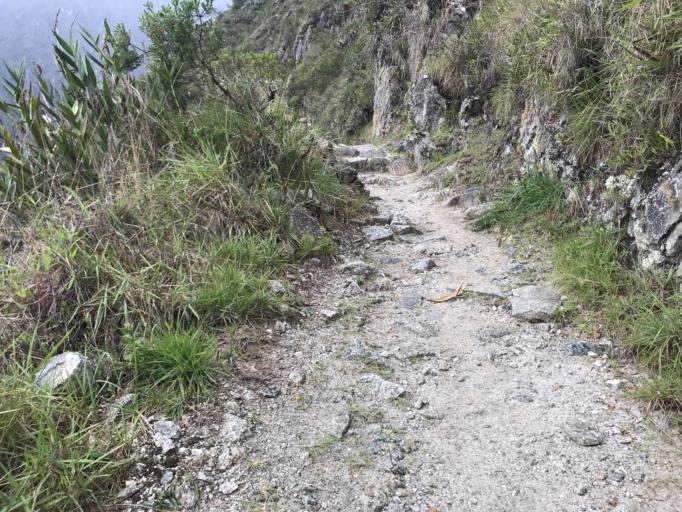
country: PE
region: Cusco
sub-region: Provincia de La Convencion
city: Santa Teresa
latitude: -13.1828
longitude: -72.5399
